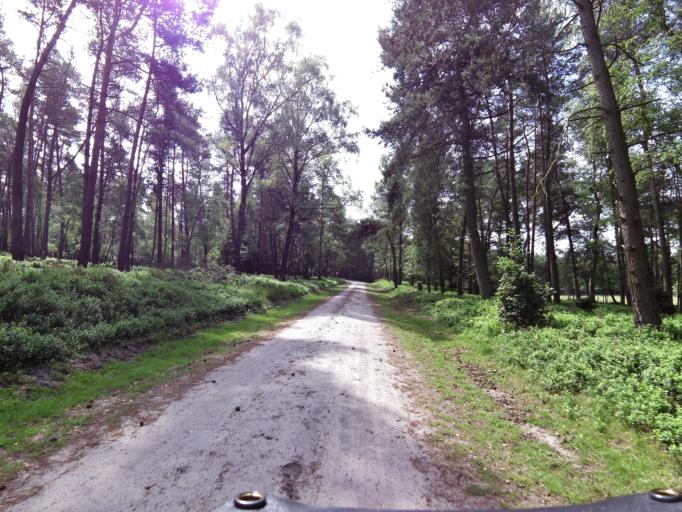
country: NL
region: Gelderland
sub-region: Gemeente Apeldoorn
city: Loenen
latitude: 52.0799
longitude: 5.9831
